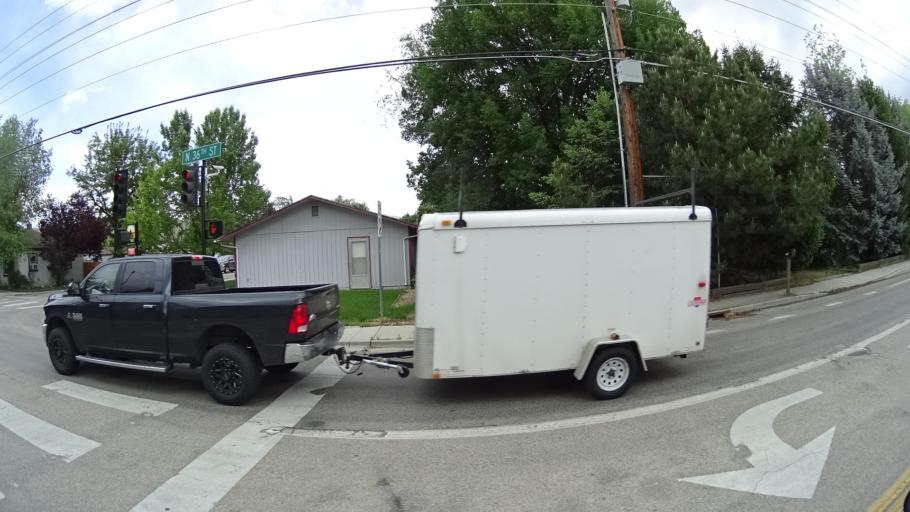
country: US
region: Idaho
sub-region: Ada County
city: Garden City
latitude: 43.6430
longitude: -116.2335
